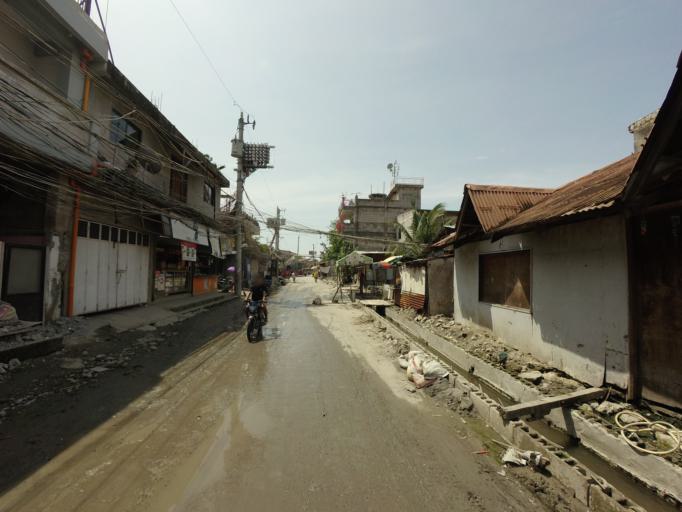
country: PH
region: Calabarzon
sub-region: Province of Rizal
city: Taguig
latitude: 14.5339
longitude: 121.1087
